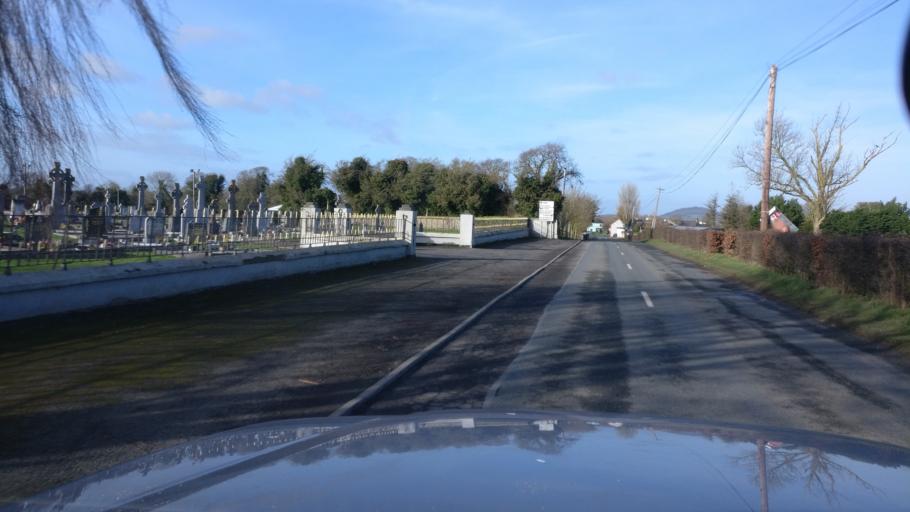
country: IE
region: Leinster
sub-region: Laois
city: Stradbally
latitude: 52.9581
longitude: -7.2000
